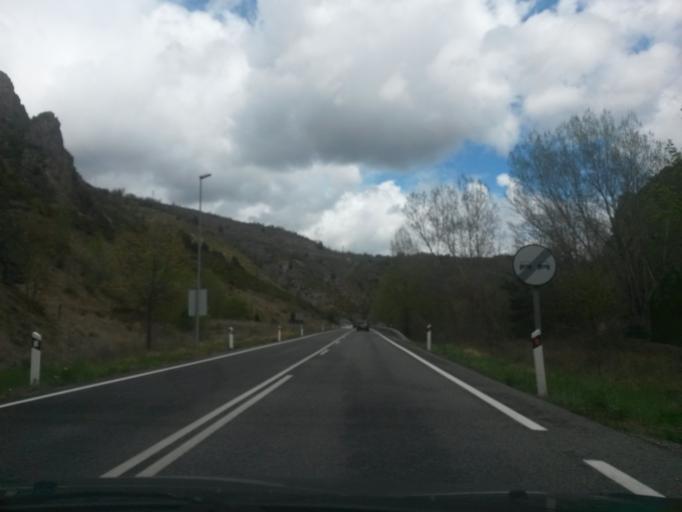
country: ES
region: Catalonia
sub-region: Provincia de Lleida
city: Lles de Cerdanya
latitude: 42.3633
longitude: 1.6706
